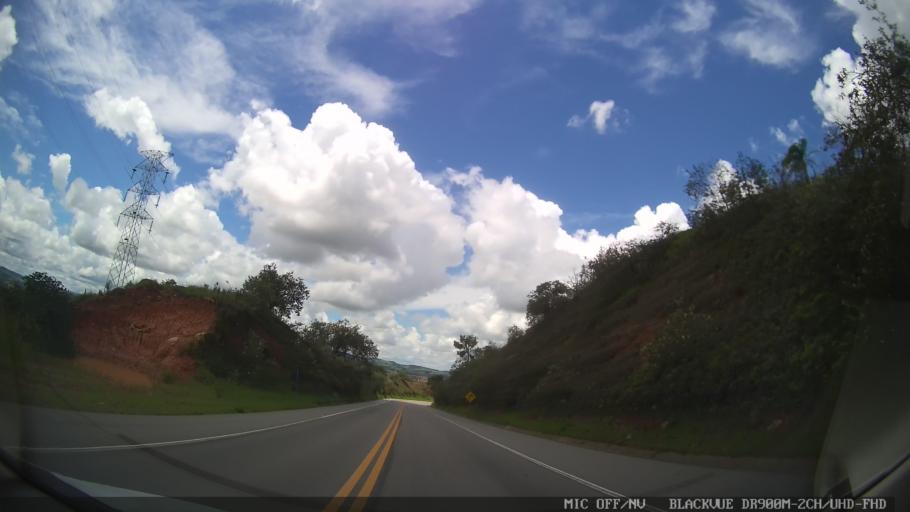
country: BR
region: Sao Paulo
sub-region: Amparo
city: Amparo
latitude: -22.7945
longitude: -46.7179
